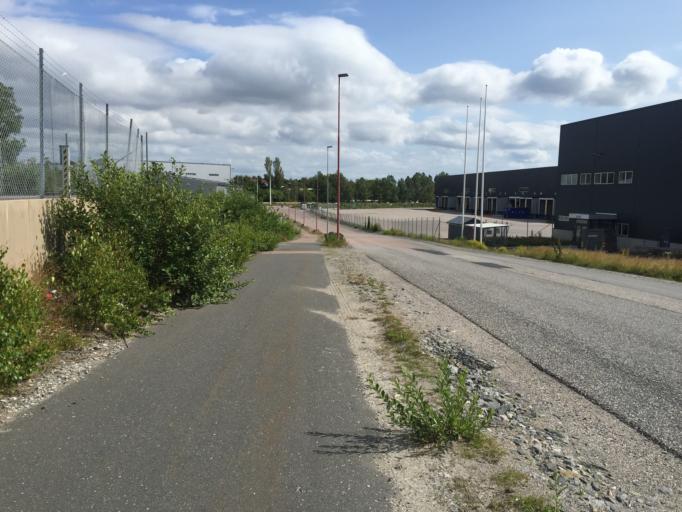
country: SE
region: Vaestra Goetaland
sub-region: Goteborg
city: Torslanda
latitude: 57.7024
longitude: 11.8263
